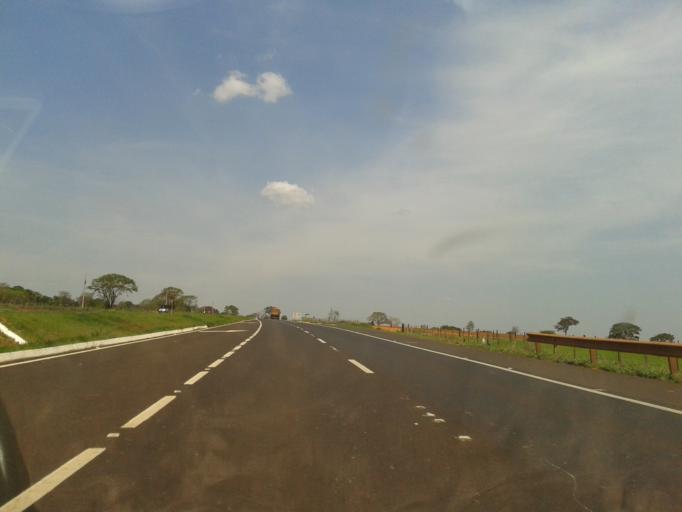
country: BR
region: Minas Gerais
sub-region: Monte Alegre De Minas
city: Monte Alegre de Minas
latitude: -18.8741
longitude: -48.7514
